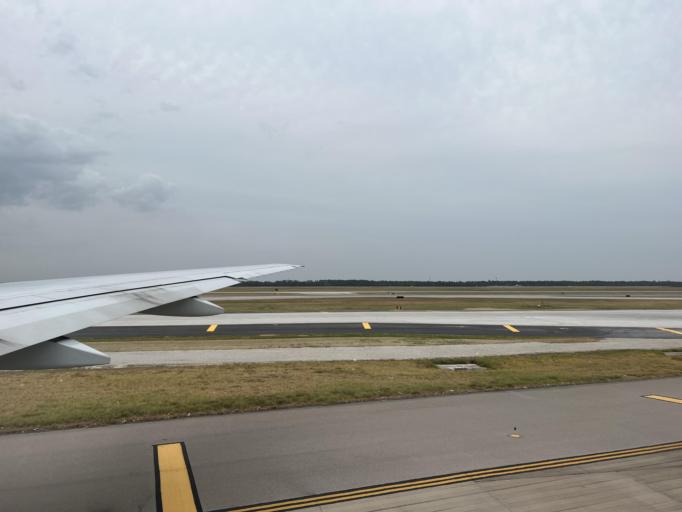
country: US
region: Texas
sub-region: Harris County
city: Aldine
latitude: 29.9908
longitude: -95.3408
